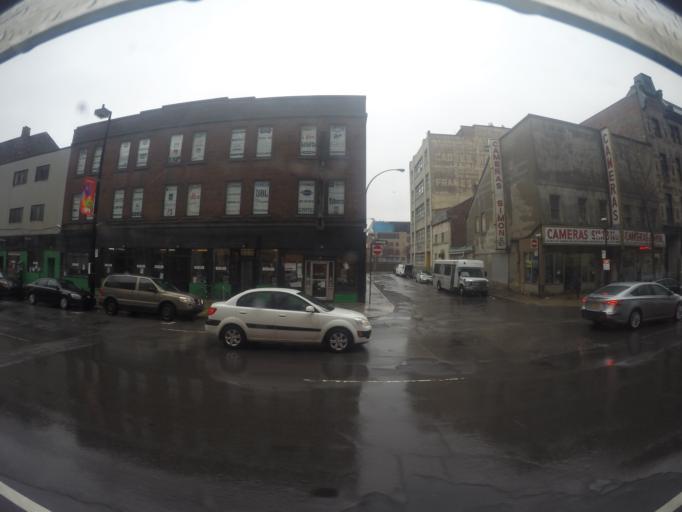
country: CA
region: Quebec
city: Saint-Raymond
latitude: 45.4463
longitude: -73.6242
